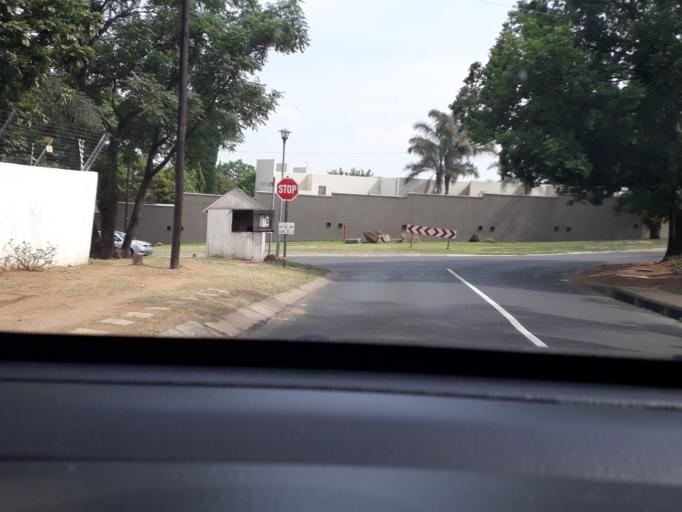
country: ZA
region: Gauteng
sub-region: City of Johannesburg Metropolitan Municipality
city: Midrand
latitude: -26.0695
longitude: 28.0539
